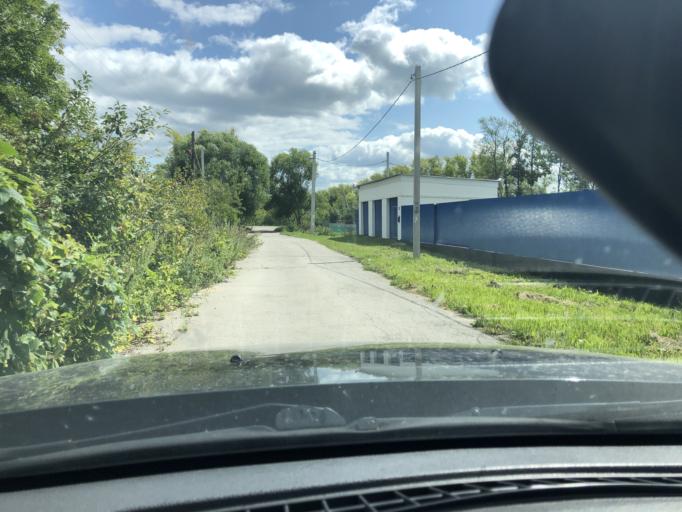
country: RU
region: Tula
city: Revyakino
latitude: 54.3477
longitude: 37.6171
